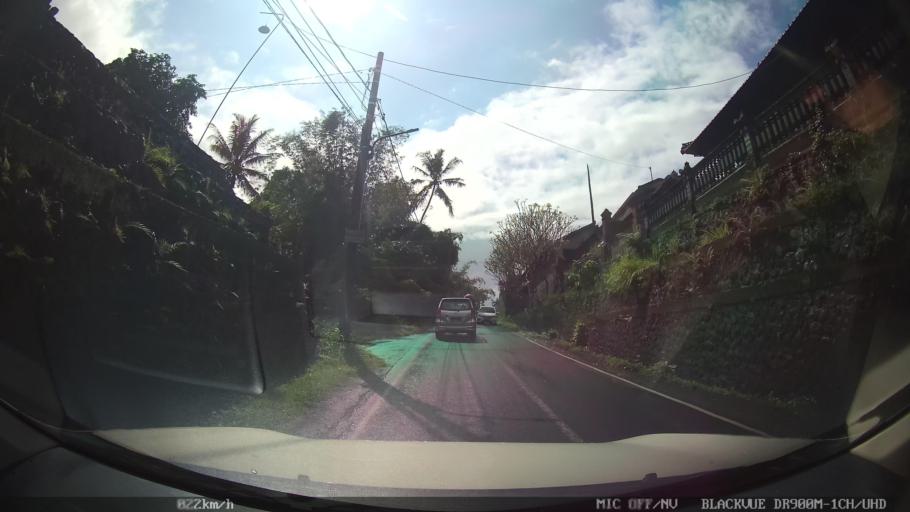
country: ID
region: Bali
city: Banjar Tebongkang
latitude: -8.5454
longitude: 115.2553
